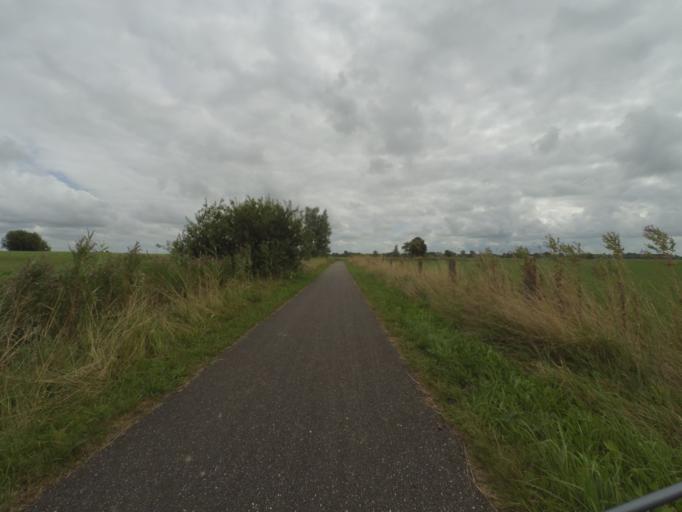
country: NL
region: Friesland
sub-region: Gemeente Kollumerland en Nieuwkruisland
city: Kollumerzwaag
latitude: 53.2947
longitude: 6.1034
